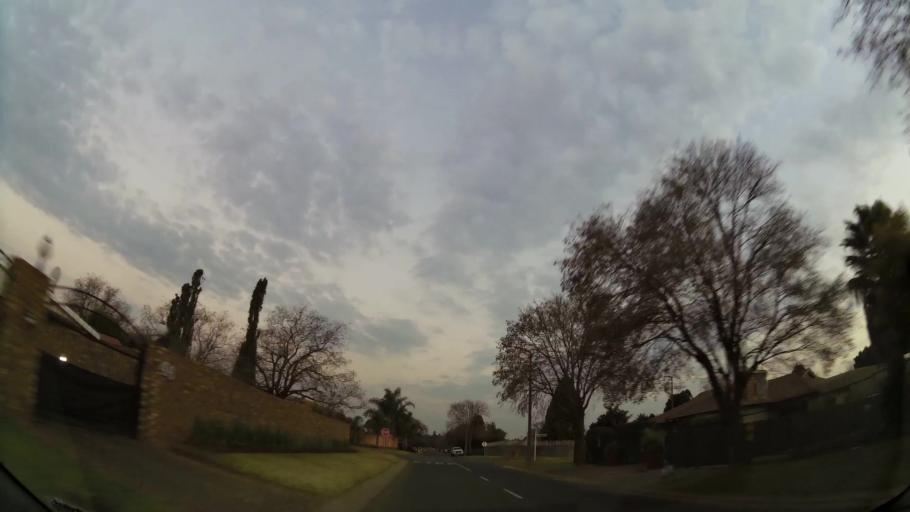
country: ZA
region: Gauteng
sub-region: Ekurhuleni Metropolitan Municipality
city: Benoni
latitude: -26.1437
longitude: 28.3063
